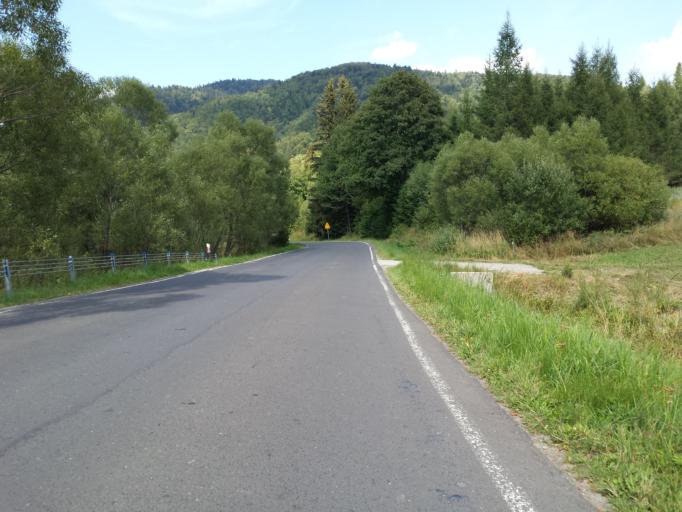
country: PL
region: Subcarpathian Voivodeship
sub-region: Powiat leski
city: Cisna
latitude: 49.1855
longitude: 22.3850
